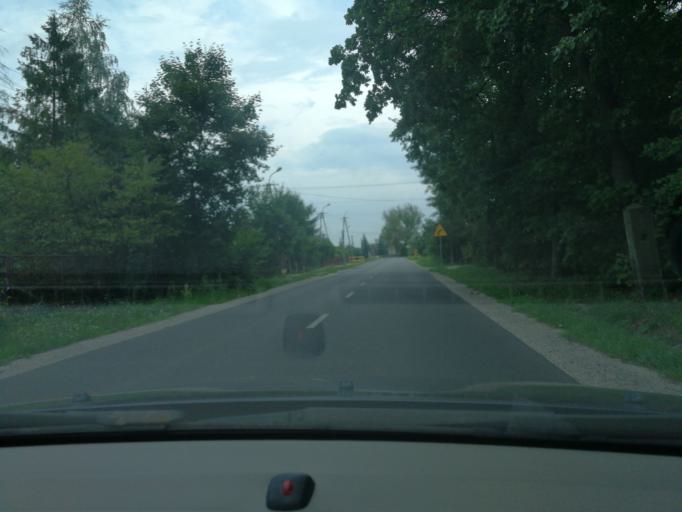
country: PL
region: Masovian Voivodeship
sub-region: Powiat grodziski
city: Grodzisk Mazowiecki
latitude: 52.1197
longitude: 20.5722
